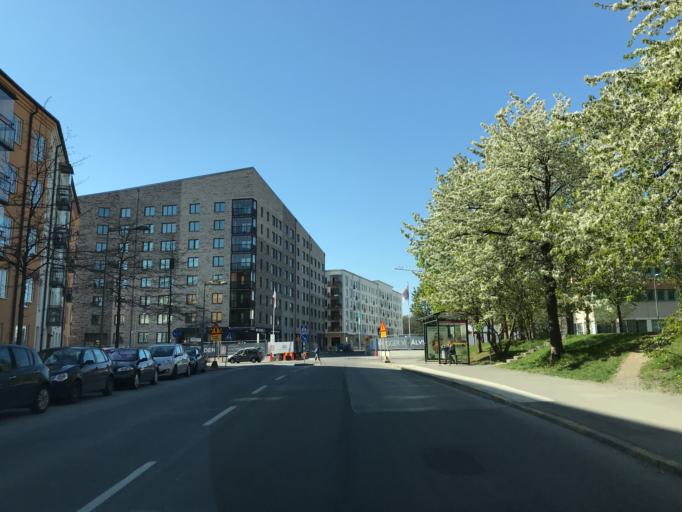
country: SE
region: Stockholm
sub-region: Huddinge Kommun
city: Huddinge
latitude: 59.2798
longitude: 18.0057
